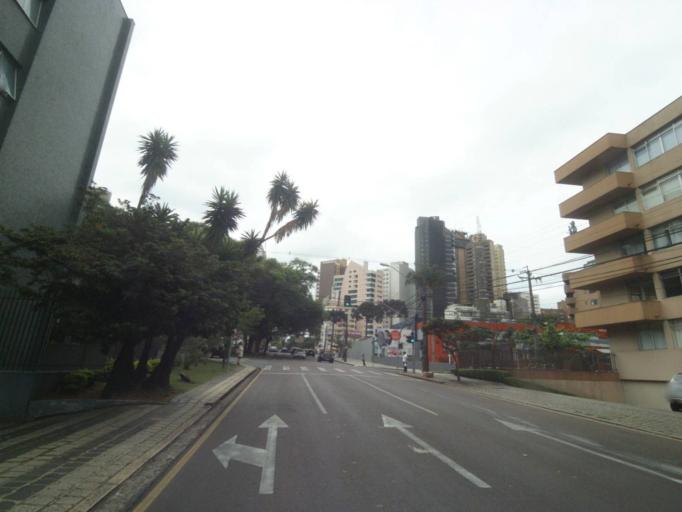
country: BR
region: Parana
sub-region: Curitiba
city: Curitiba
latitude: -25.4330
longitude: -49.2919
